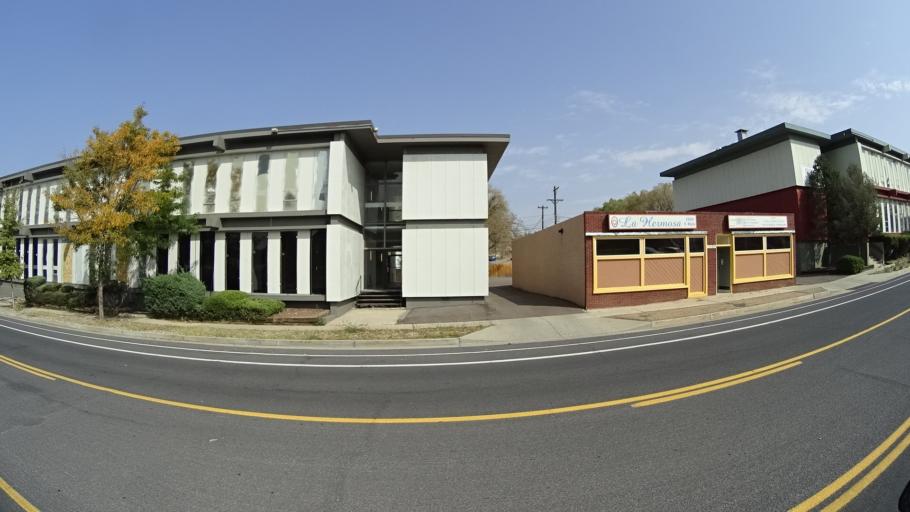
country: US
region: Colorado
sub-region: El Paso County
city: Colorado Springs
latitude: 38.8355
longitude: -104.7886
